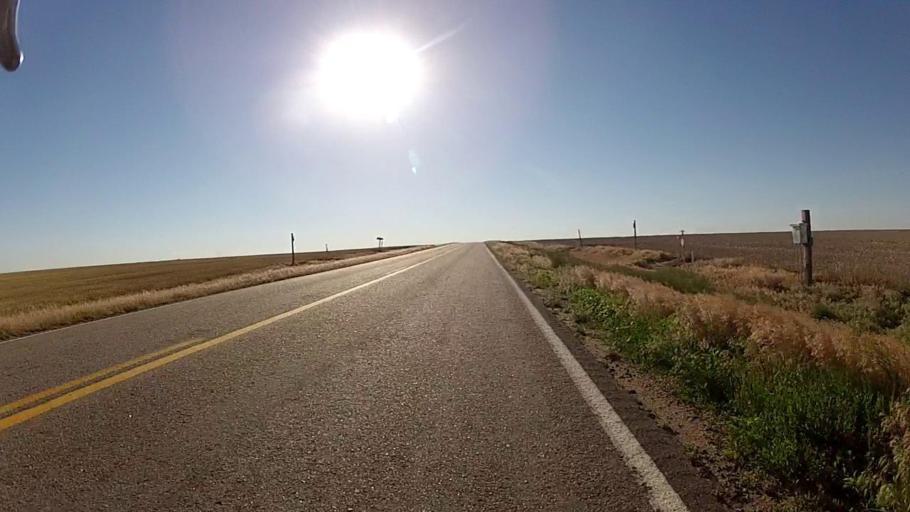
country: US
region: Kansas
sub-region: Ford County
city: Dodge City
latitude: 37.6462
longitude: -99.8318
